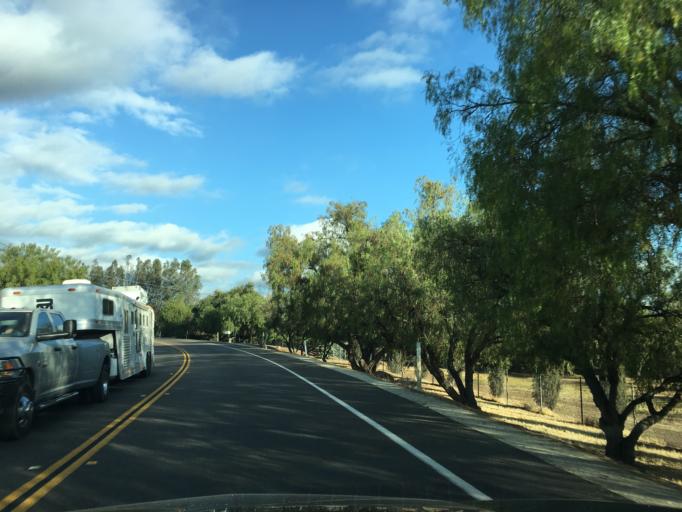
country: US
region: California
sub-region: San Diego County
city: Valley Center
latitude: 33.2341
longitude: -117.0495
